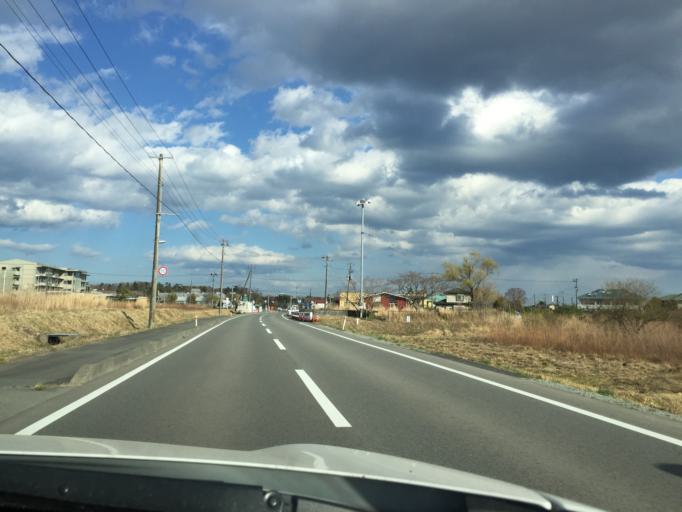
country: JP
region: Fukushima
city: Namie
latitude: 37.4103
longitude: 140.9775
